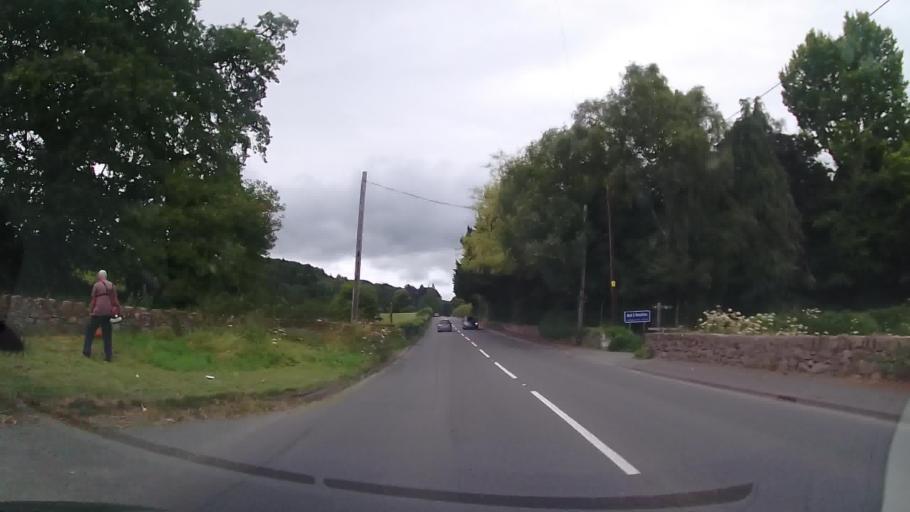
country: GB
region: Wales
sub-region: Wrexham
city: Chirk
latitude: 52.9579
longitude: -3.0703
